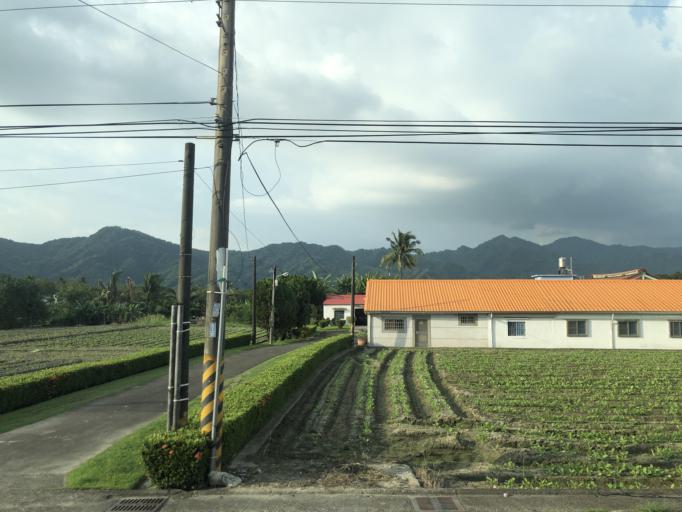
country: TW
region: Taiwan
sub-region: Pingtung
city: Pingtung
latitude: 22.8866
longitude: 120.5264
